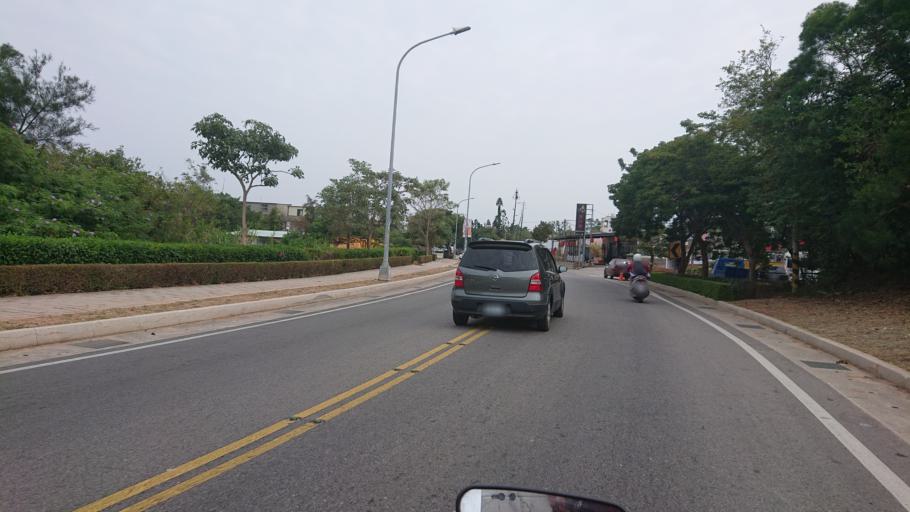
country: TW
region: Fukien
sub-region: Kinmen
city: Jincheng
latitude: 24.4236
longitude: 118.3145
